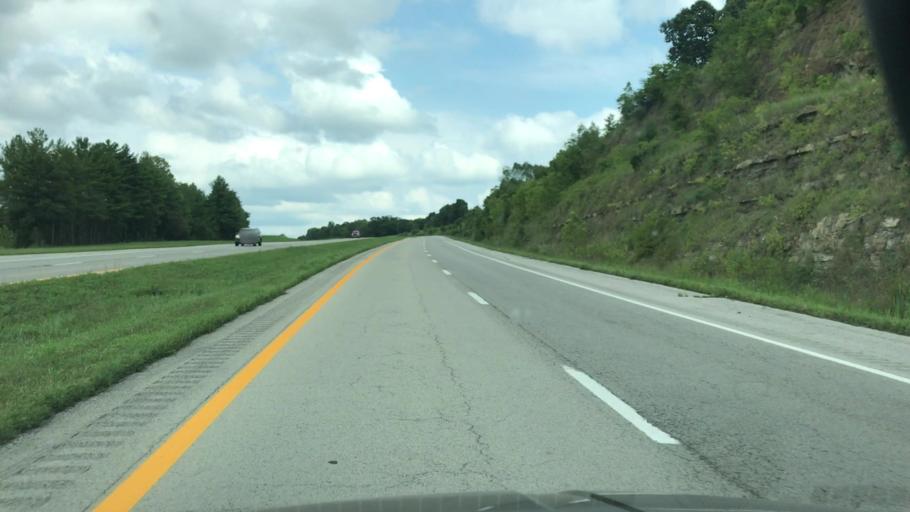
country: US
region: Kentucky
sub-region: Caldwell County
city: Princeton
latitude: 37.1406
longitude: -87.8200
